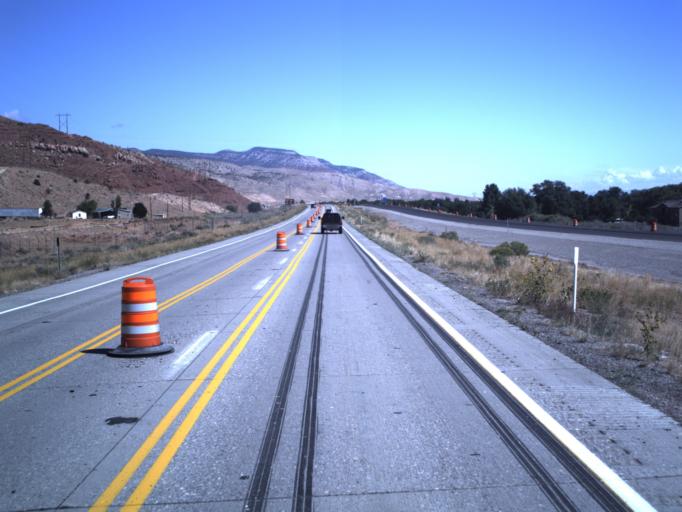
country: US
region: Utah
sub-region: Sevier County
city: Richfield
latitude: 38.7663
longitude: -112.1026
